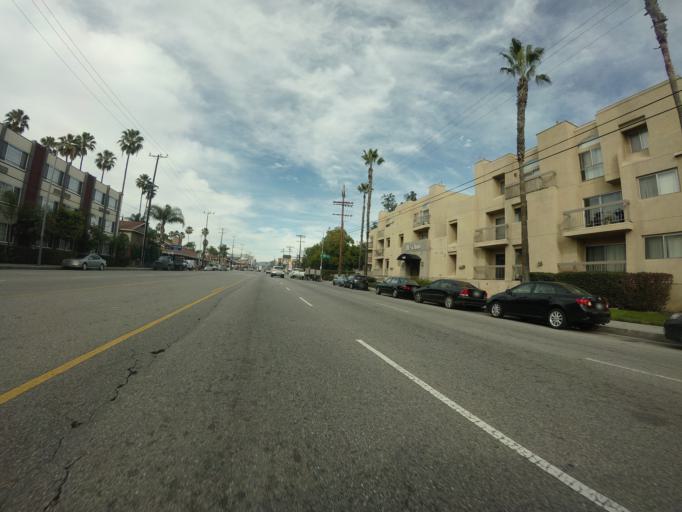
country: US
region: California
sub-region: Los Angeles County
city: Van Nuys
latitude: 34.1705
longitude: -118.4661
